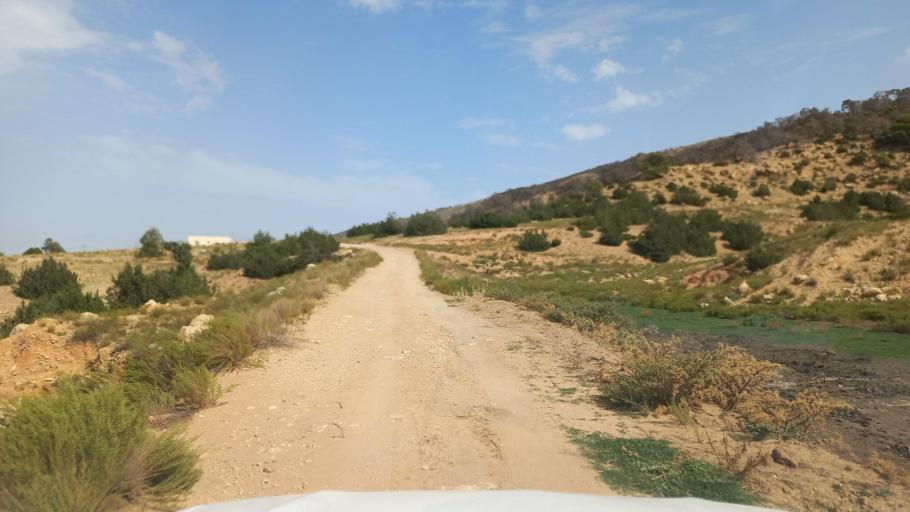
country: TN
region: Al Qasrayn
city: Kasserine
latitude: 35.3532
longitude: 8.8893
